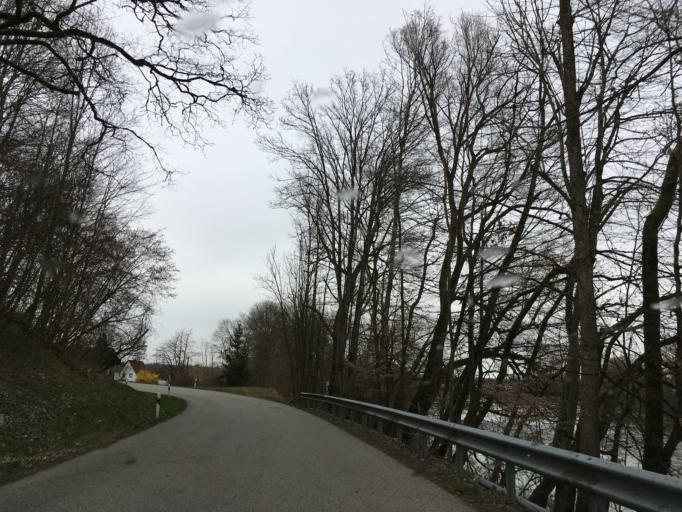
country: DE
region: Bavaria
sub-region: Upper Bavaria
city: Jettenbach
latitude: 48.1701
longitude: 12.3840
